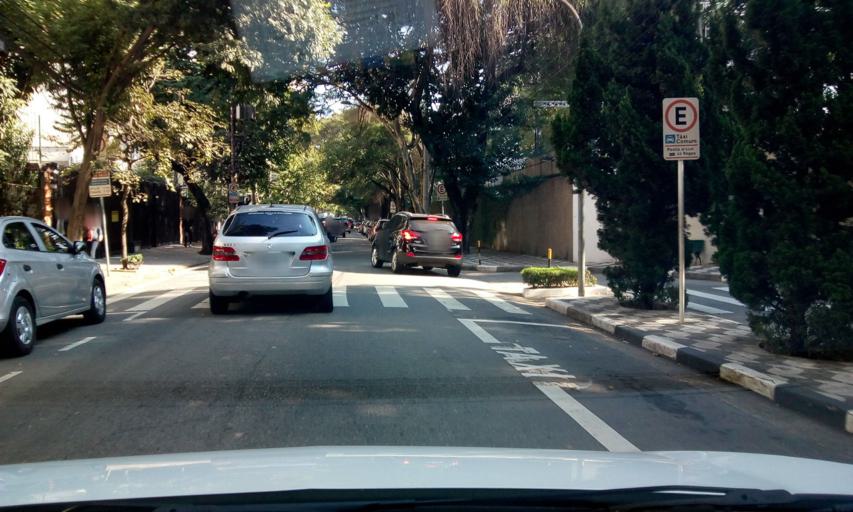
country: BR
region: Sao Paulo
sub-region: Sao Paulo
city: Sao Paulo
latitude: -23.5802
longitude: -46.6864
